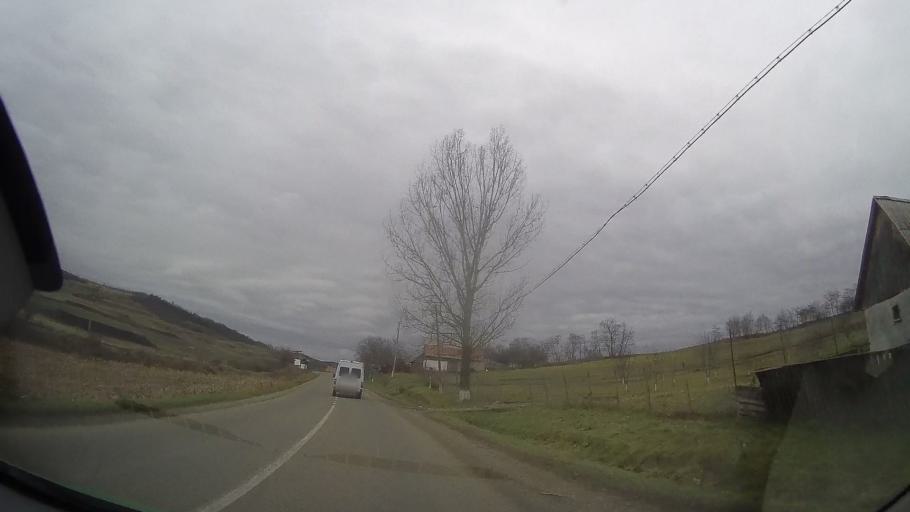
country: RO
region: Cluj
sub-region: Comuna Catina
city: Catina
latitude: 46.7982
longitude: 24.2133
